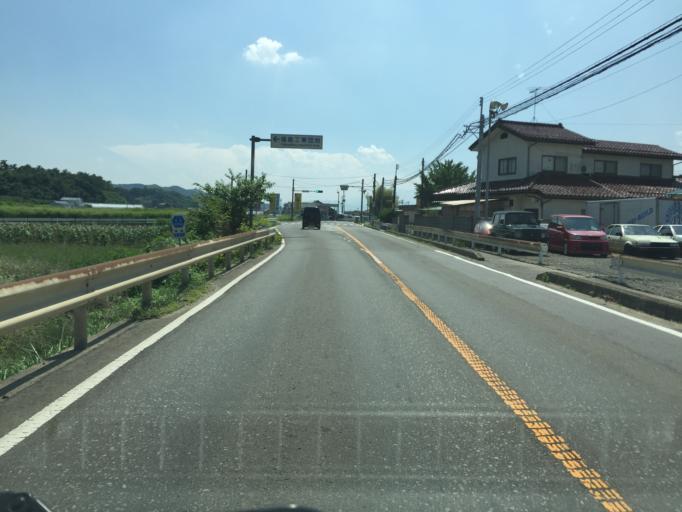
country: JP
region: Fukushima
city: Hobaramachi
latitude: 37.7926
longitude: 140.5143
